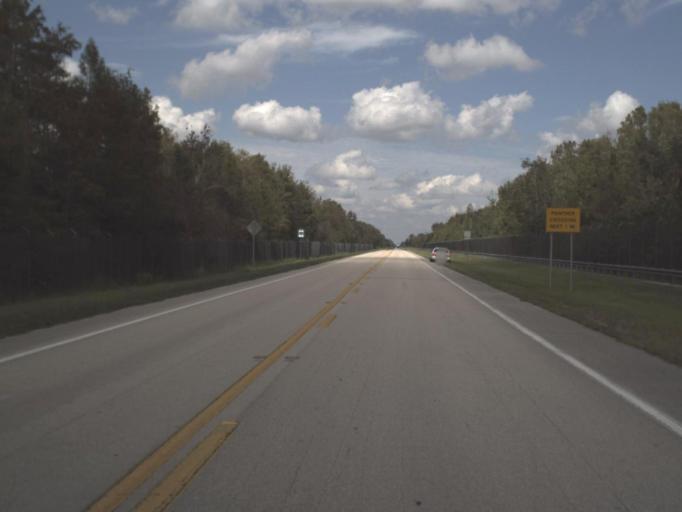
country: US
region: Florida
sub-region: Collier County
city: Orangetree
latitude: 26.0538
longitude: -81.3445
